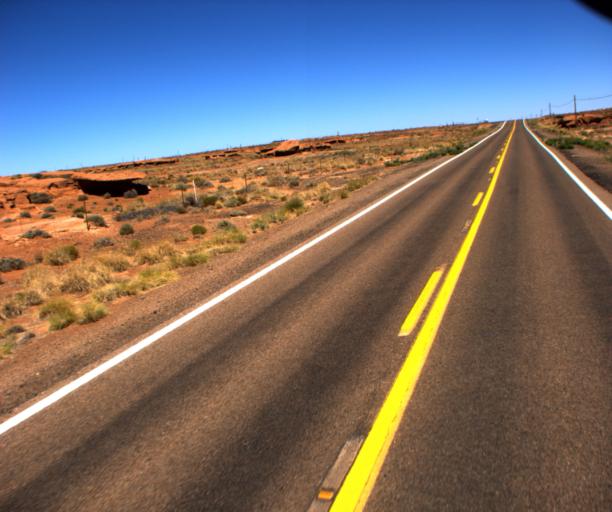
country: US
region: Arizona
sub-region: Navajo County
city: Winslow
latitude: 34.9893
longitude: -110.6661
